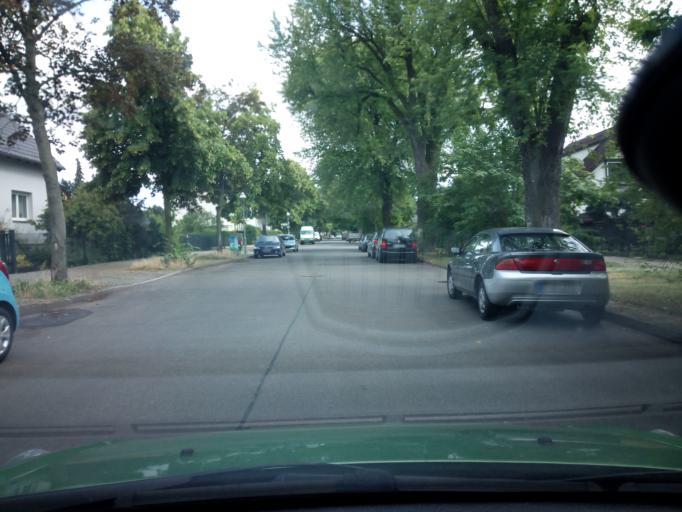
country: DE
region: Berlin
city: Rudow
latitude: 52.4276
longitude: 13.4949
